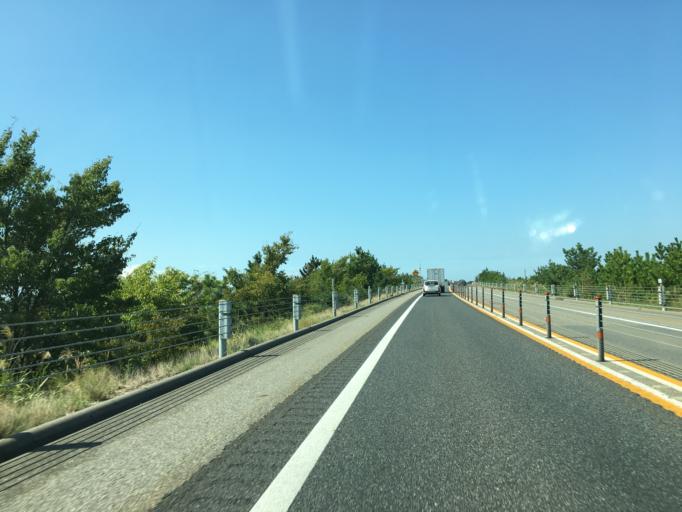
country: JP
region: Niigata
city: Kameda-honcho
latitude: 37.8297
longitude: 139.0746
